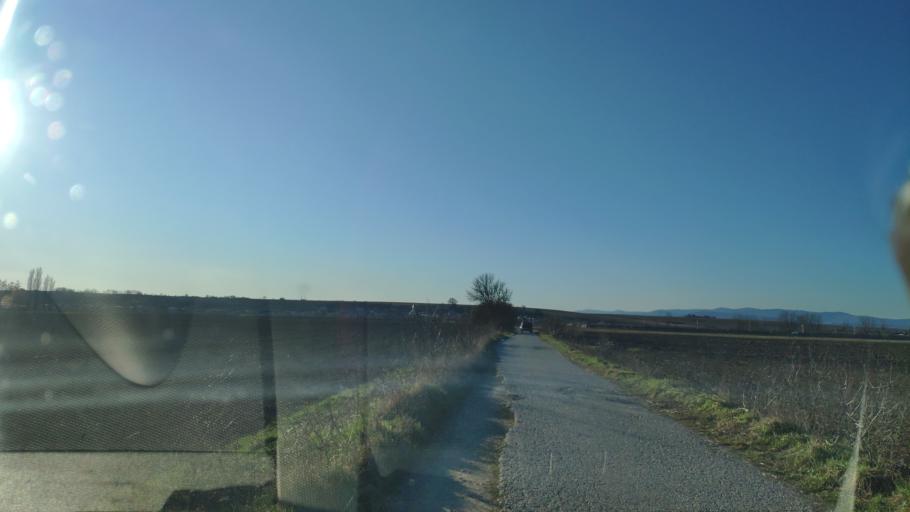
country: HU
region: Borsod-Abauj-Zemplen
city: Gonc
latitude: 48.5880
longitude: 21.3188
